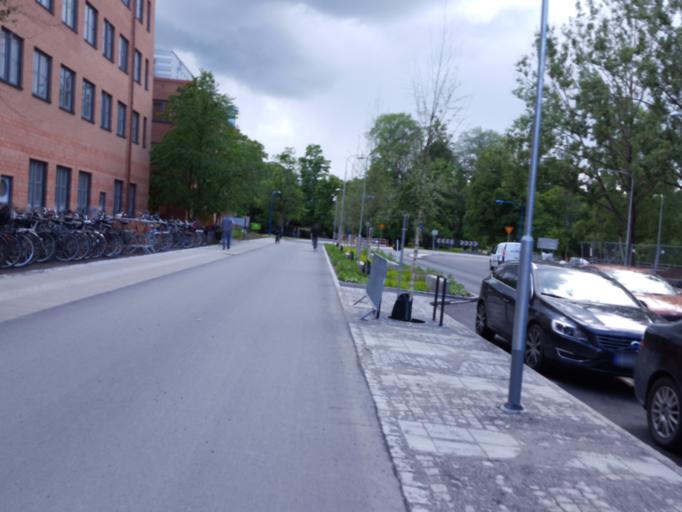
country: SE
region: Uppsala
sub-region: Uppsala Kommun
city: Uppsala
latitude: 59.8526
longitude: 17.6472
